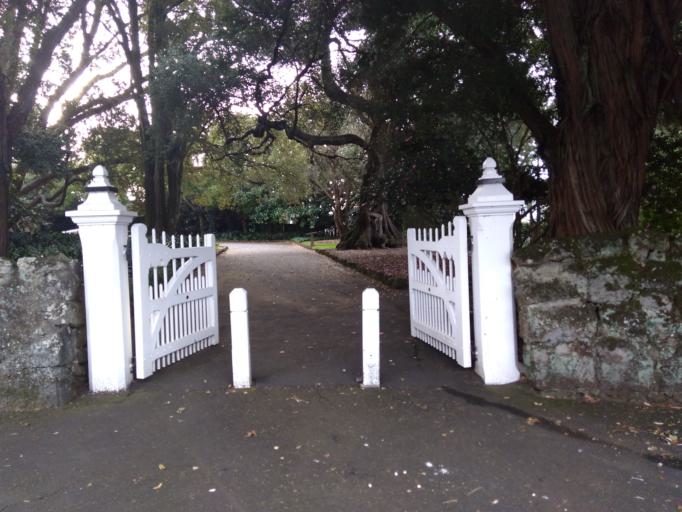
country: NZ
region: Auckland
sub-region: Auckland
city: Auckland
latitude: -36.8810
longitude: 174.7229
